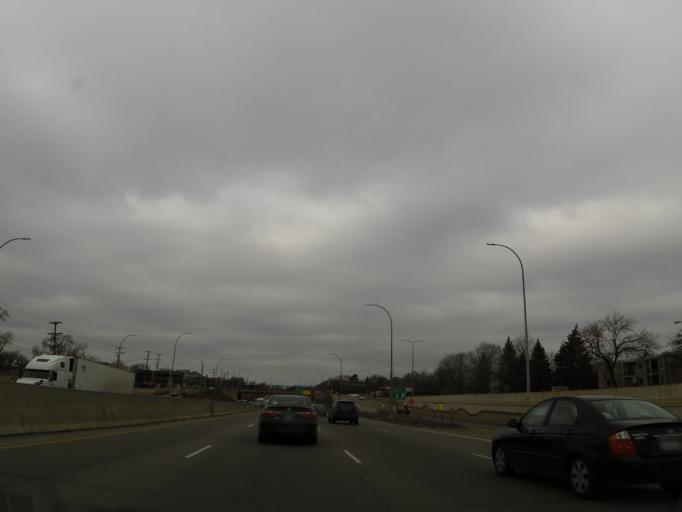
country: US
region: Minnesota
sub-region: Hennepin County
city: Richfield
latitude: 44.8625
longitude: -93.2538
